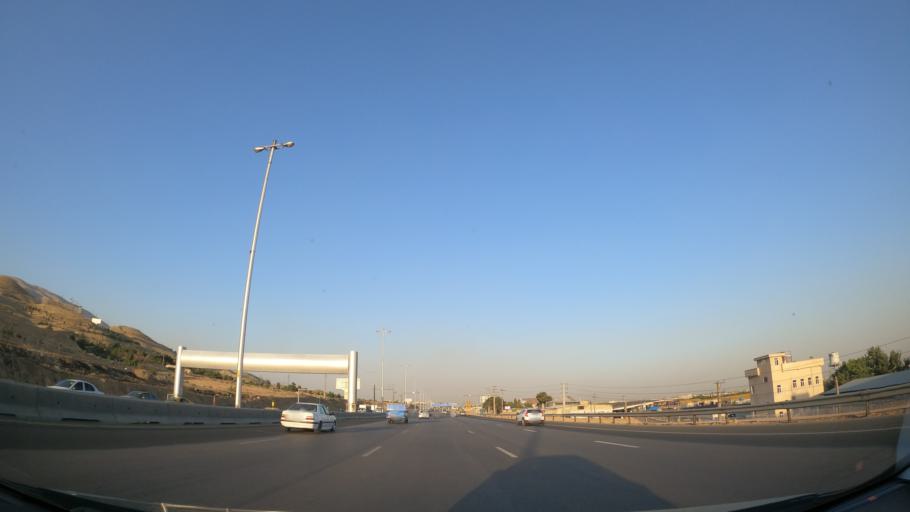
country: IR
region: Tehran
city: Shahr-e Qods
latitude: 35.7434
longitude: 51.1020
